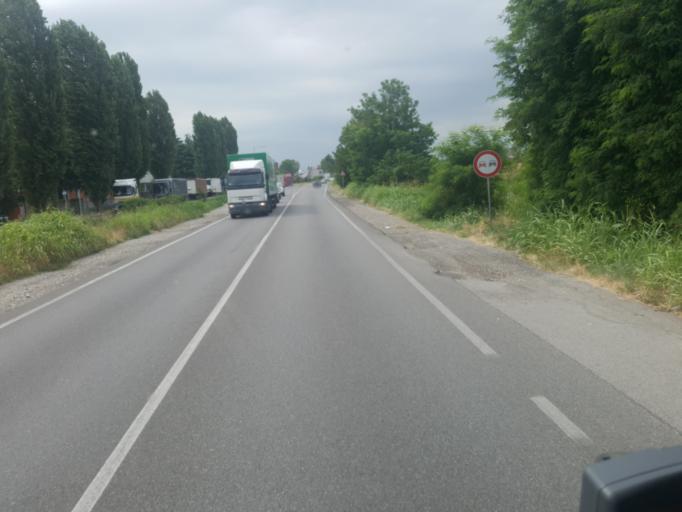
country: IT
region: Lombardy
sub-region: Citta metropolitana di Milano
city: Melzo
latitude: 45.5069
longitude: 9.4118
